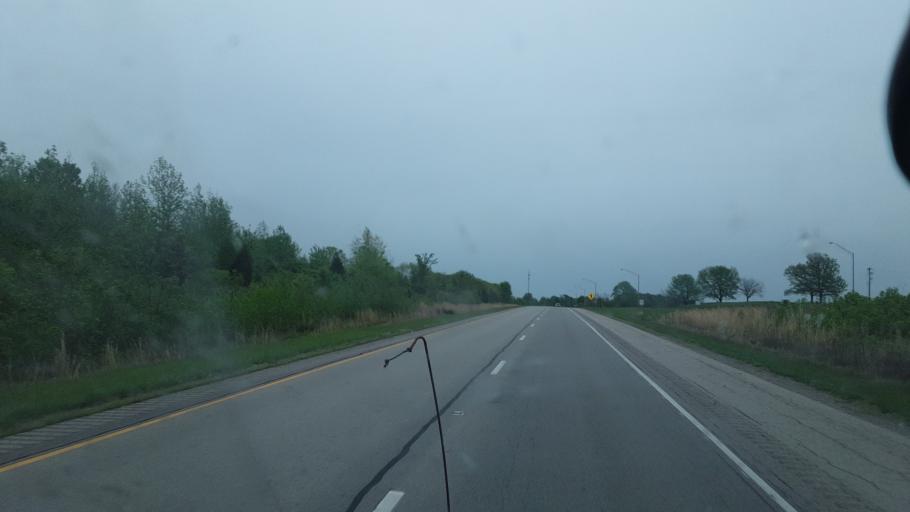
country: US
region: Indiana
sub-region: Spencer County
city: Dale
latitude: 38.1954
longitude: -86.9490
